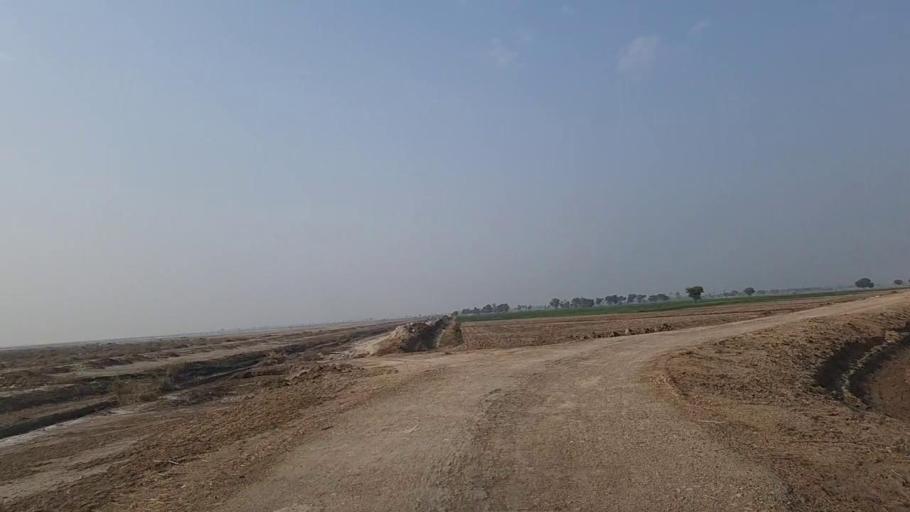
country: PK
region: Sindh
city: Nawabshah
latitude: 26.3341
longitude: 68.4737
